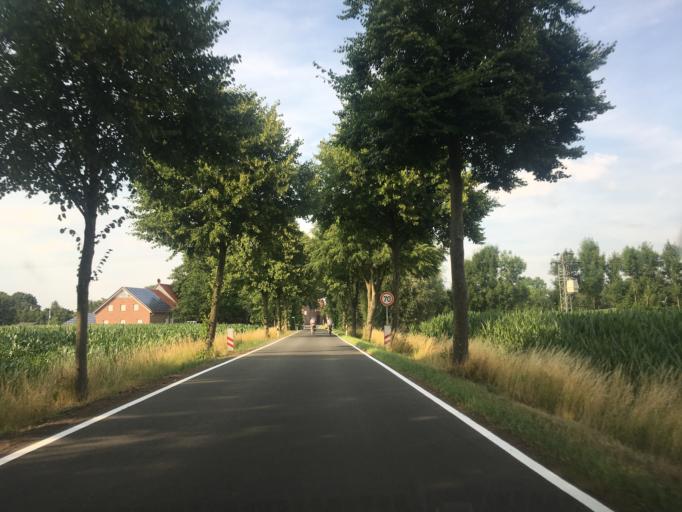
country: DE
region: North Rhine-Westphalia
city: Ludinghausen
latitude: 51.7942
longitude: 7.3737
